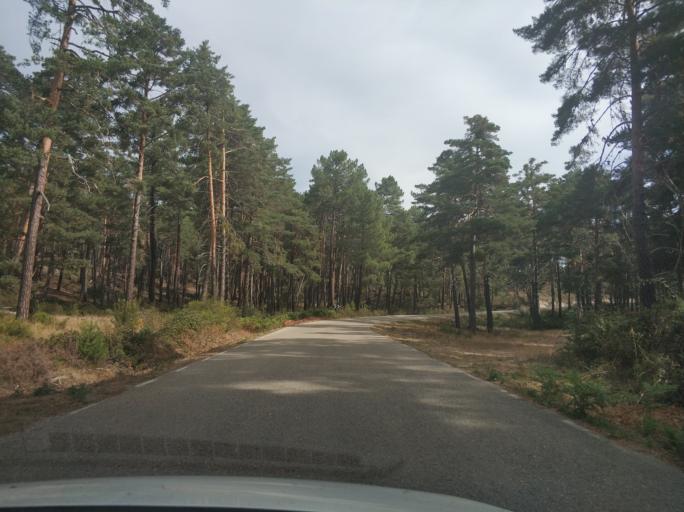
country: ES
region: Castille and Leon
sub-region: Provincia de Soria
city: Navaleno
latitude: 41.8483
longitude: -2.9889
